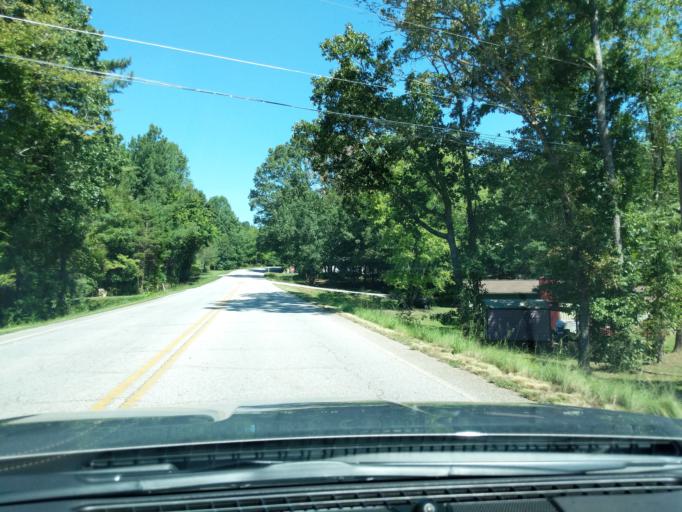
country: US
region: Georgia
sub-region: Habersham County
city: Demorest
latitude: 34.5929
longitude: -83.6191
